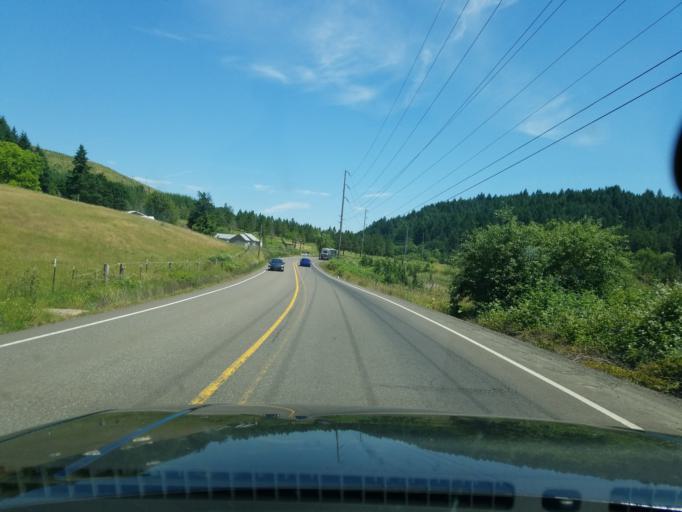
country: US
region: Oregon
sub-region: Yamhill County
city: Yamhill
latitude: 45.3806
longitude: -123.1450
